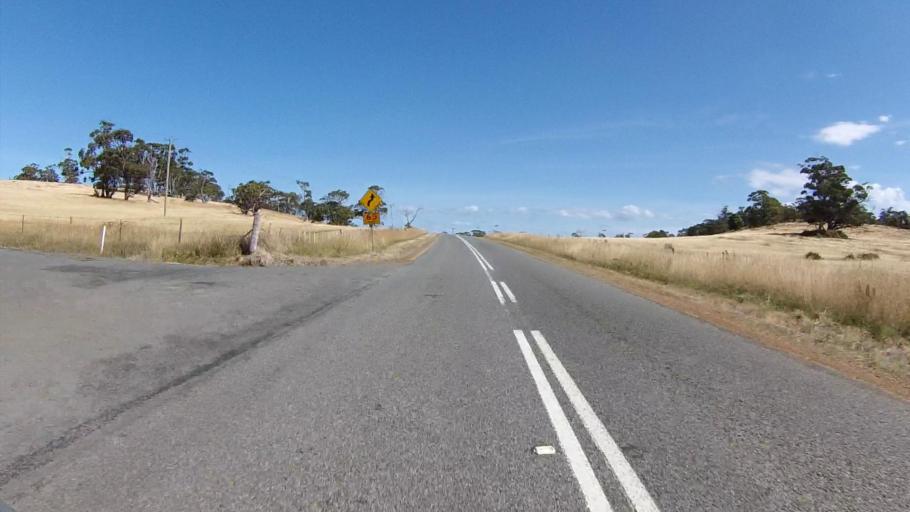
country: AU
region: Tasmania
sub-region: Sorell
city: Sorell
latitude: -42.2989
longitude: 147.9822
